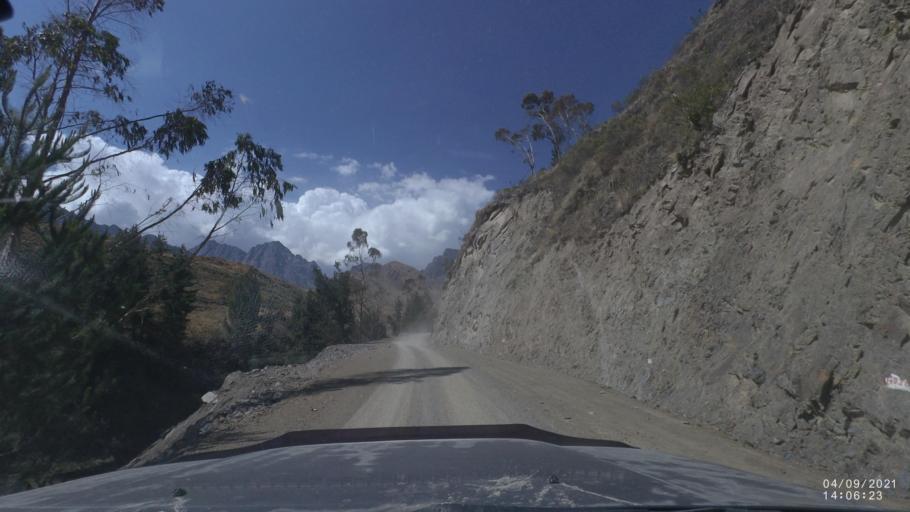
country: BO
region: Cochabamba
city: Sipe Sipe
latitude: -17.2308
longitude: -66.4716
